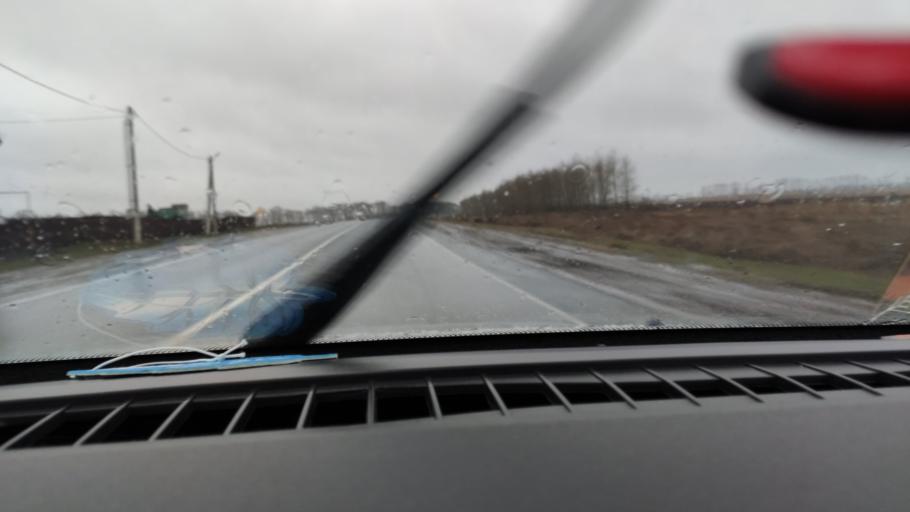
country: RU
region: Tatarstan
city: Mendeleyevsk
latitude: 55.8528
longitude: 52.2109
